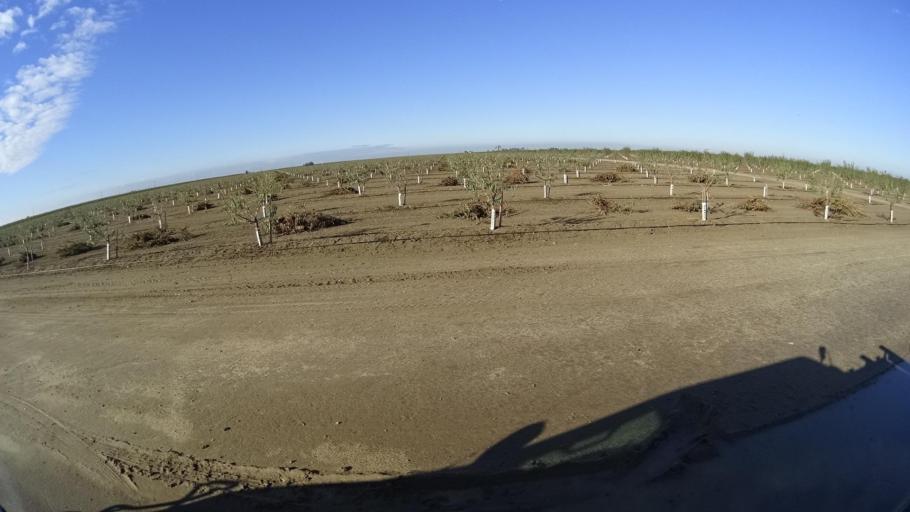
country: US
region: California
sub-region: Kern County
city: Delano
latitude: 35.7139
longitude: -119.2941
